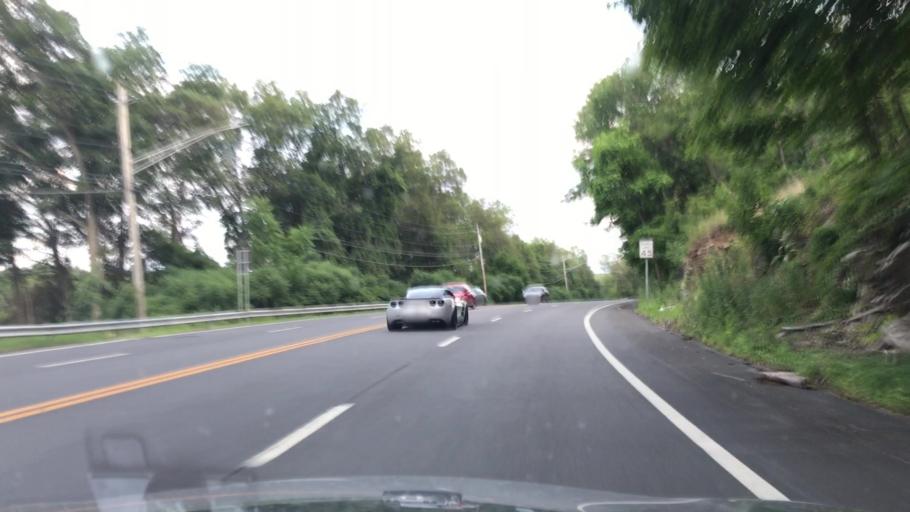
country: US
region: New York
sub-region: Rockland County
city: Sloatsburg
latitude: 41.1865
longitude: -74.1834
